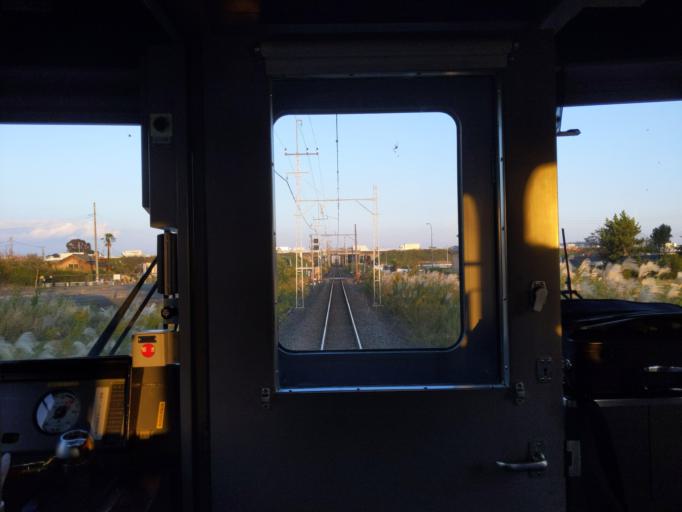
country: JP
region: Saitama
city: Kasukabe
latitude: 35.9803
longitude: 139.7905
